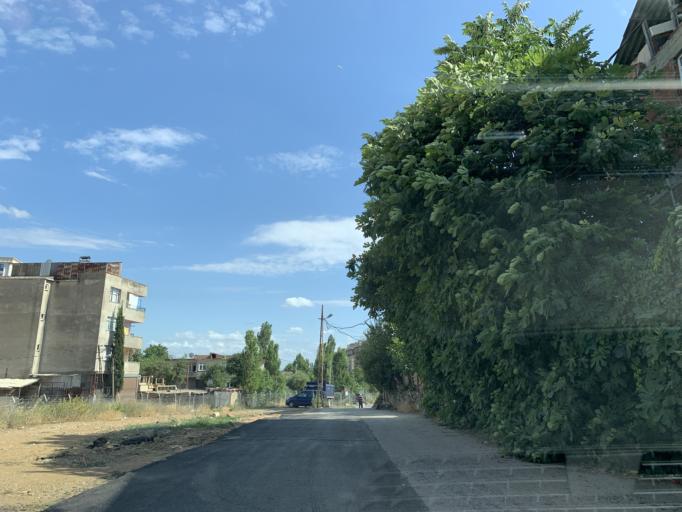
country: TR
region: Istanbul
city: Pendik
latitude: 40.8897
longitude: 29.2747
